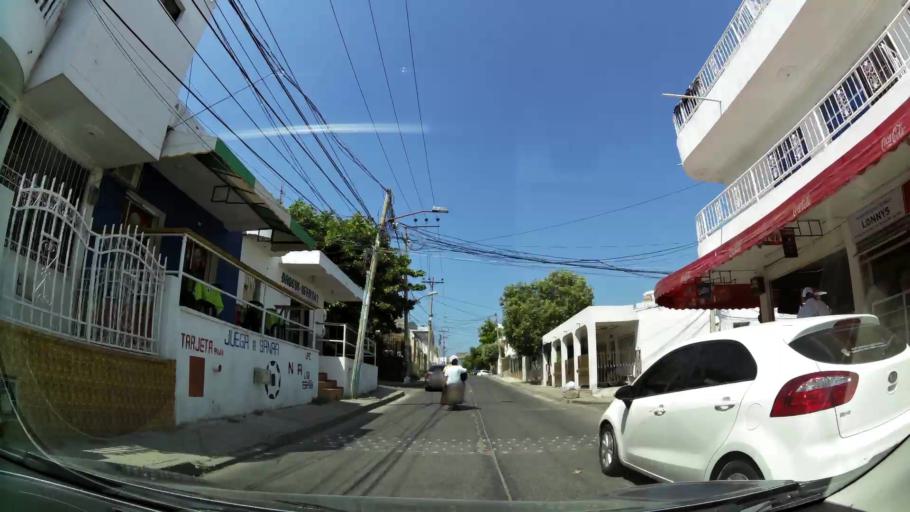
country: CO
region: Bolivar
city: Cartagena
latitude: 10.3929
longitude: -75.4914
